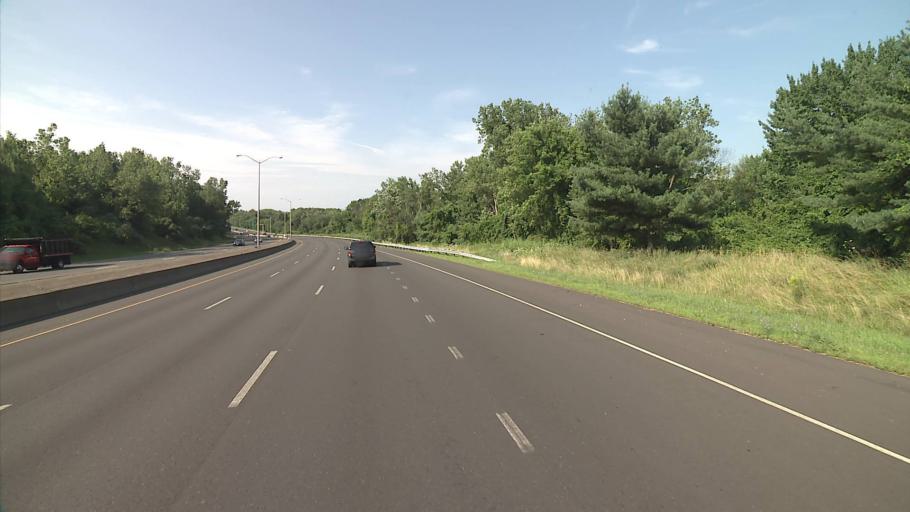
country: US
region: Connecticut
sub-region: Hartford County
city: Enfield
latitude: 41.9508
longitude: -72.6042
